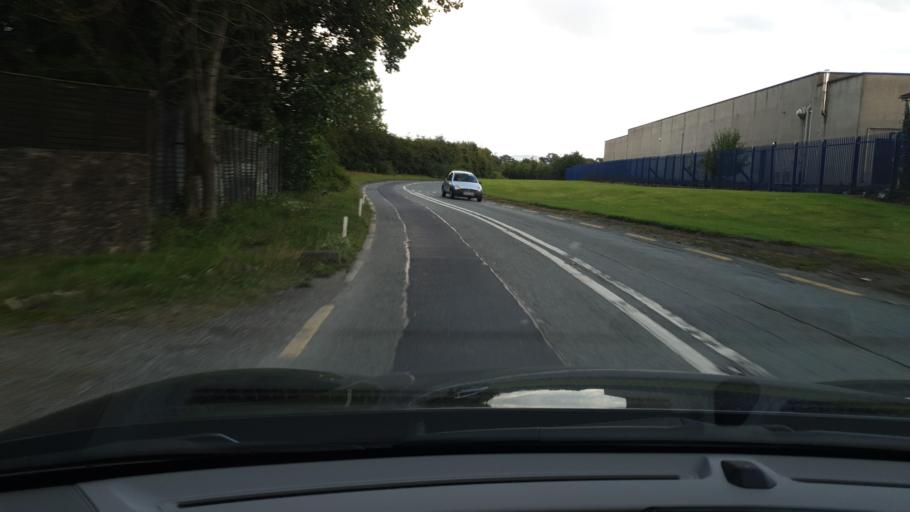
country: IE
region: Leinster
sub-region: South Dublin
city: Saggart
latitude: 53.3077
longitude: -6.4386
